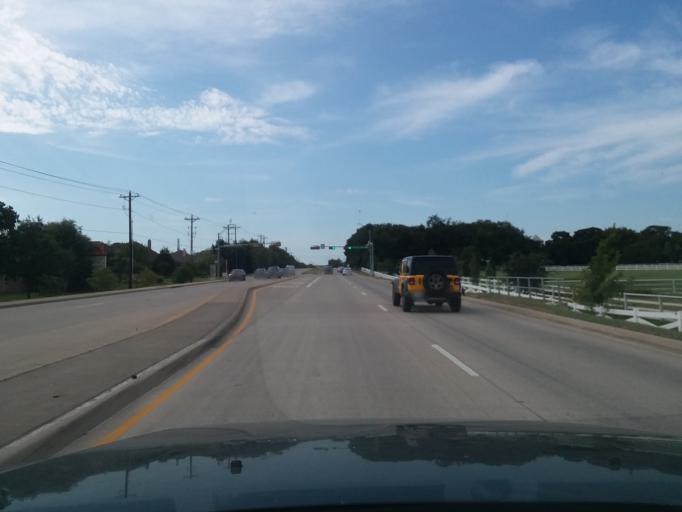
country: US
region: Texas
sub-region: Denton County
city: Bartonville
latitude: 33.0956
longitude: -97.1313
